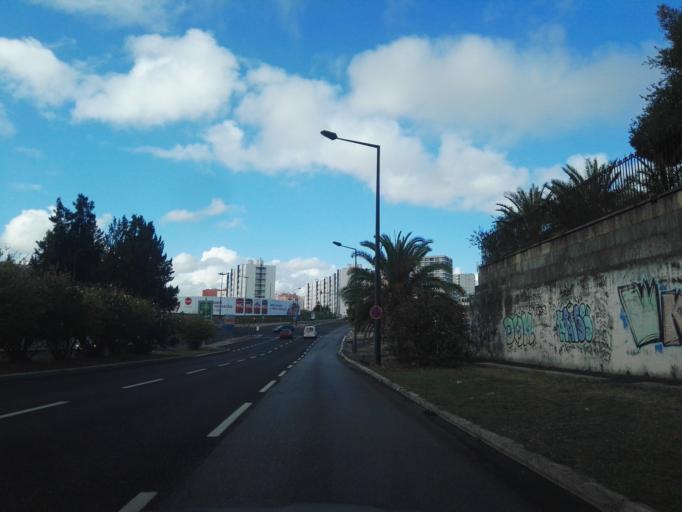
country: PT
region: Lisbon
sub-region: Odivelas
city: Pontinha
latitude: 38.7492
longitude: -9.1645
